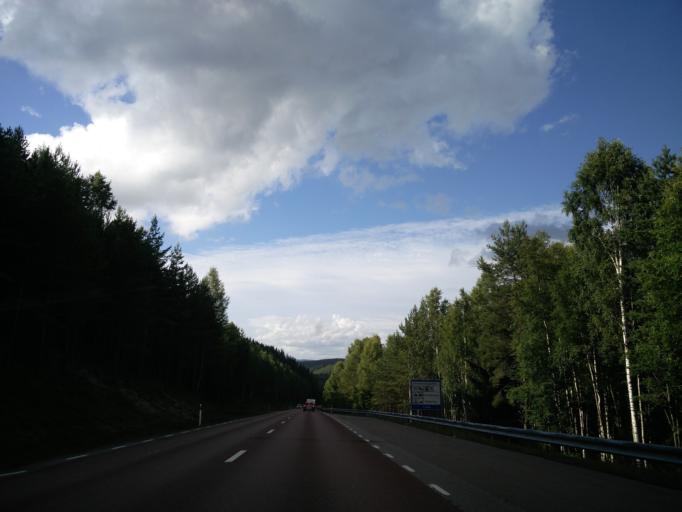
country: SE
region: Vaermland
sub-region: Hagfors Kommun
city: Ekshaerad
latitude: 60.4128
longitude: 13.2551
